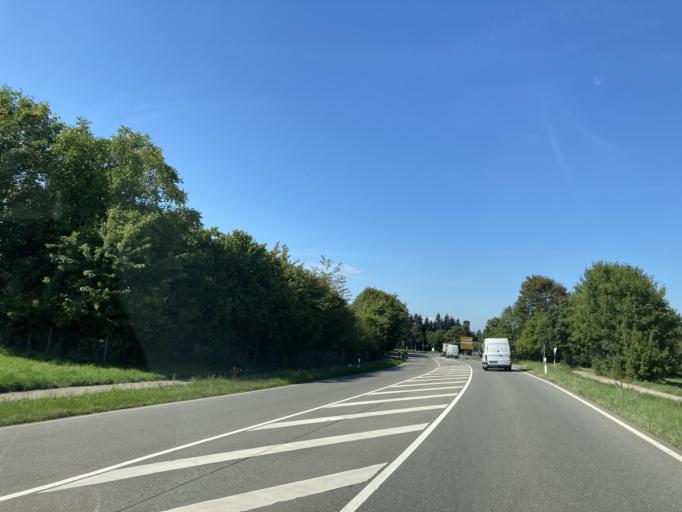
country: DE
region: Baden-Wuerttemberg
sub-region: Tuebingen Region
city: Riedlingen
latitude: 48.1531
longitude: 9.4987
